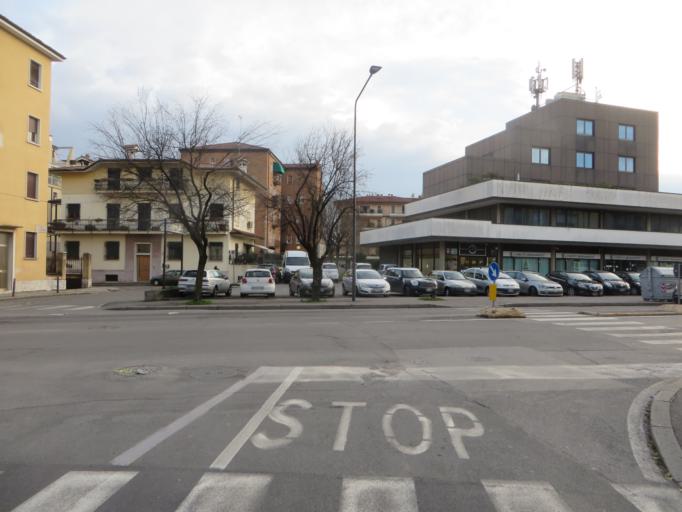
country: IT
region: Lombardy
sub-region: Provincia di Brescia
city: Brescia
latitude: 45.5310
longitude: 10.2390
